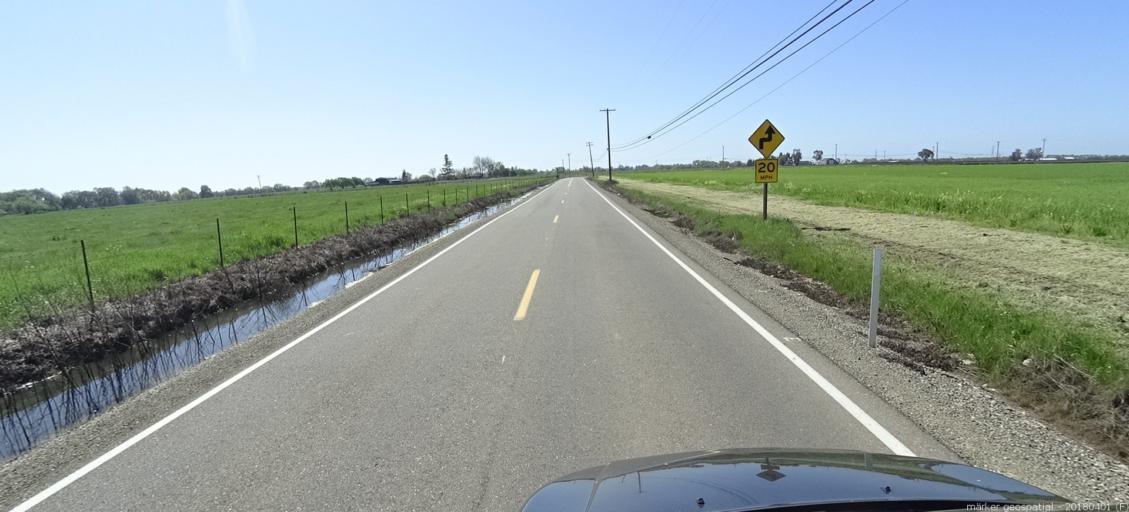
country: US
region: California
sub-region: Sacramento County
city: Herald
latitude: 38.3235
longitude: -121.2237
